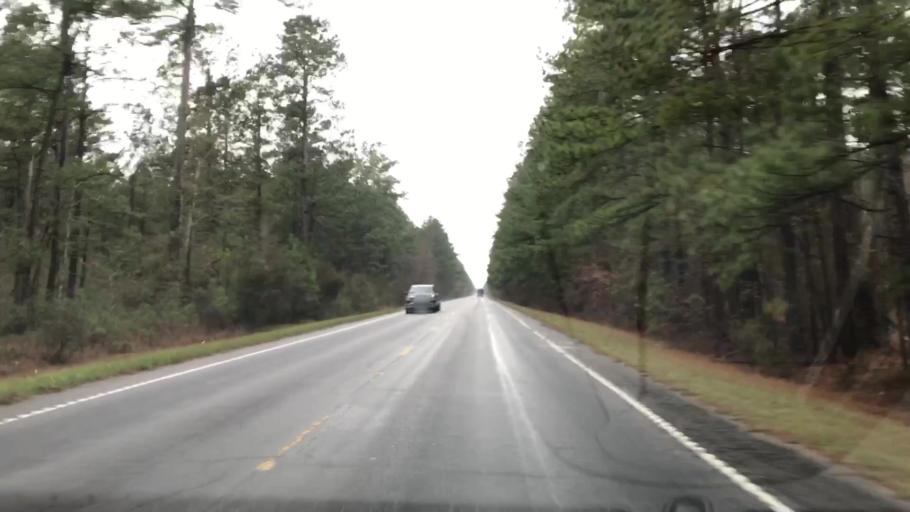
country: US
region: South Carolina
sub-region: Berkeley County
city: Saint Stephen
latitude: 33.2875
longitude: -79.8383
